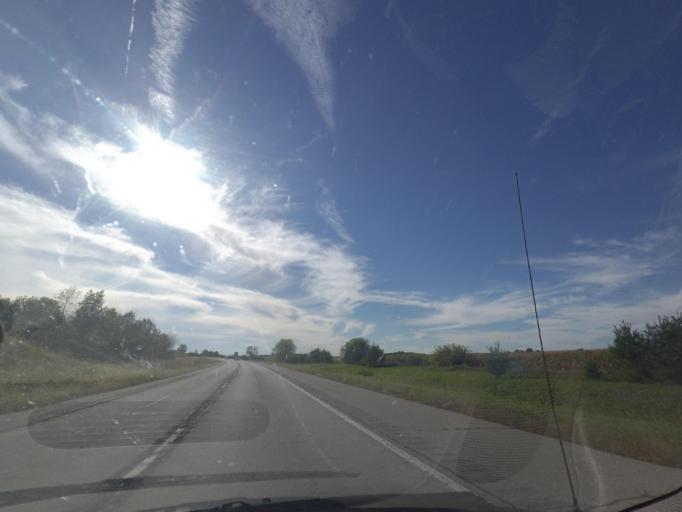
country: US
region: Illinois
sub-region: Macon County
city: Forsyth
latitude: 39.9080
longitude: -88.9845
